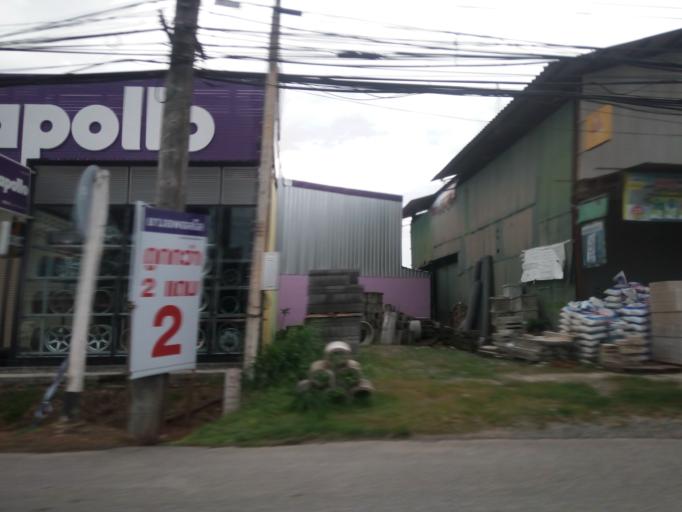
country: TH
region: Phuket
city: Thalang
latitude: 7.9945
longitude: 98.3524
